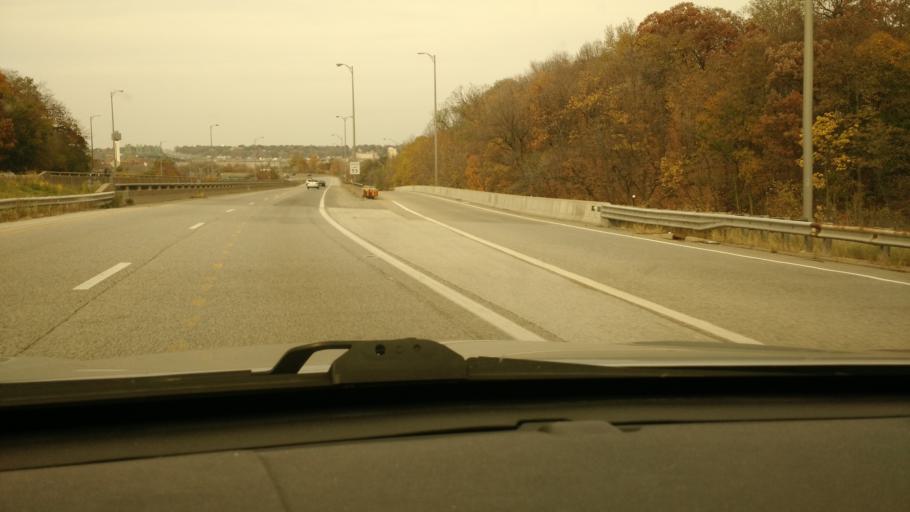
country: US
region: Illinois
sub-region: Rock Island County
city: Moline
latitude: 41.5022
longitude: -90.5082
